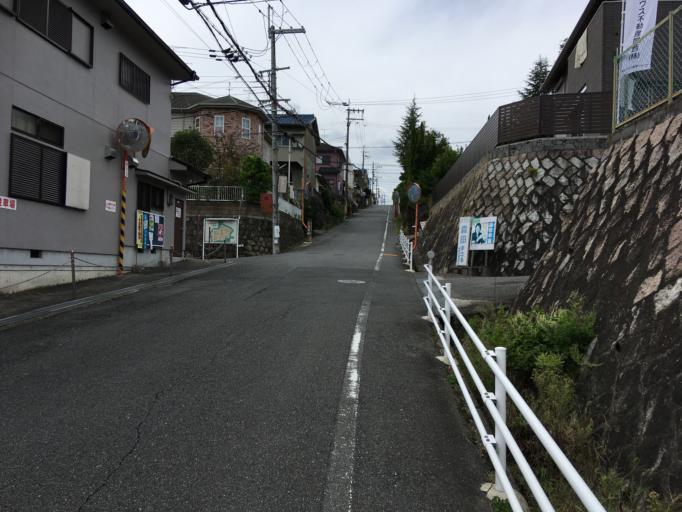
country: JP
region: Nara
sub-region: Ikoma-shi
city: Ikoma
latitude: 34.6167
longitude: 135.7028
